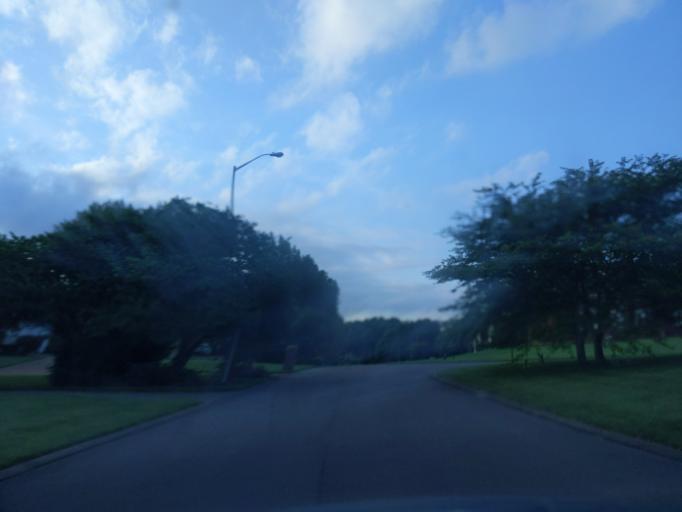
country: US
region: Tennessee
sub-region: Williamson County
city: Brentwood Estates
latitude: 36.0090
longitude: -86.7674
